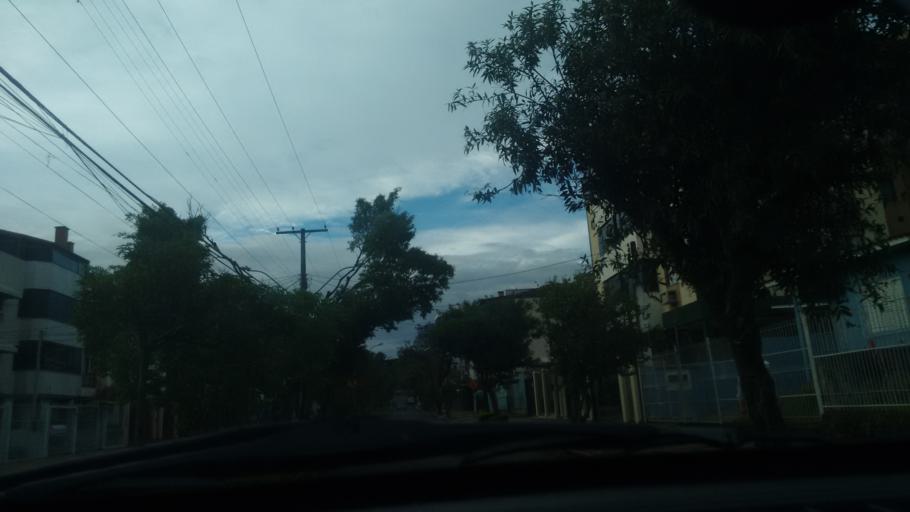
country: BR
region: Rio Grande do Sul
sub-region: Cachoeirinha
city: Cachoeirinha
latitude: -30.0011
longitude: -51.1461
